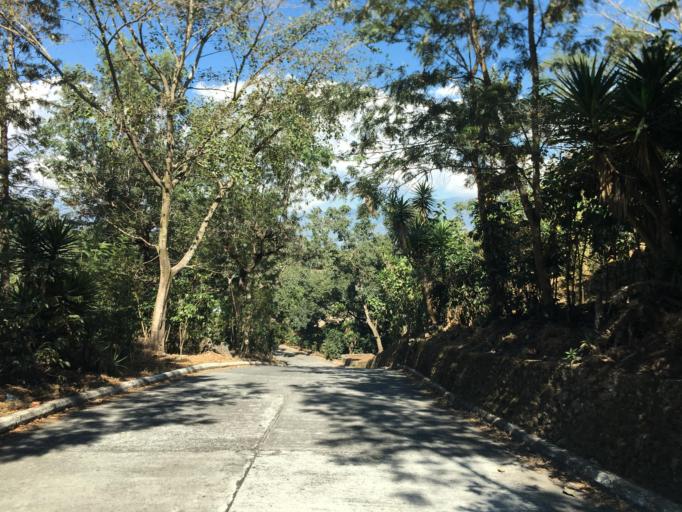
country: GT
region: Solola
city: Santa Catarina Palopo
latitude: 14.6664
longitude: -91.1716
